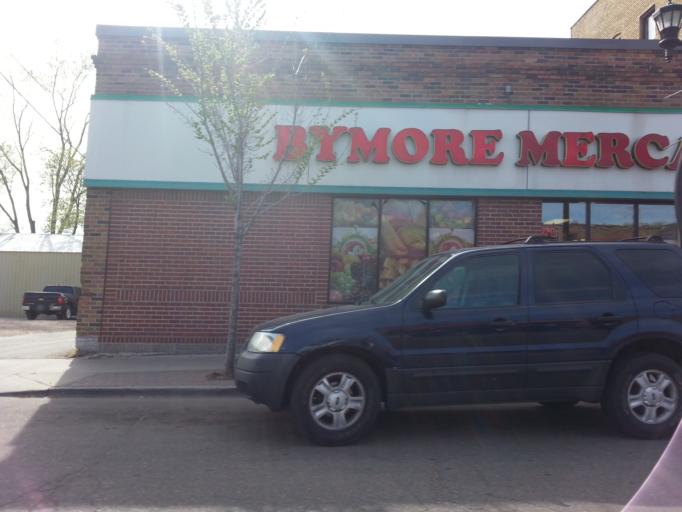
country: US
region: Minnesota
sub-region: Ramsey County
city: Saint Paul
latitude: 44.9671
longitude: -93.0736
